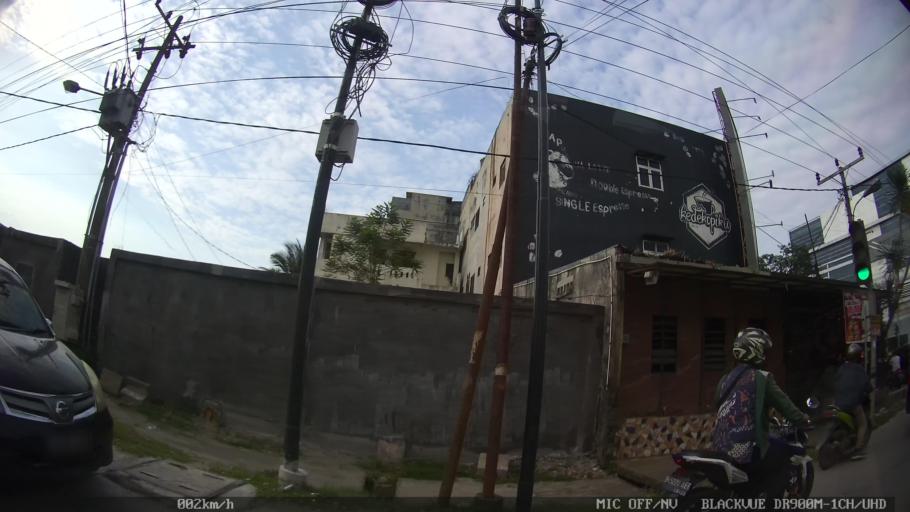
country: ID
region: North Sumatra
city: Sunggal
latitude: 3.5626
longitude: 98.6258
